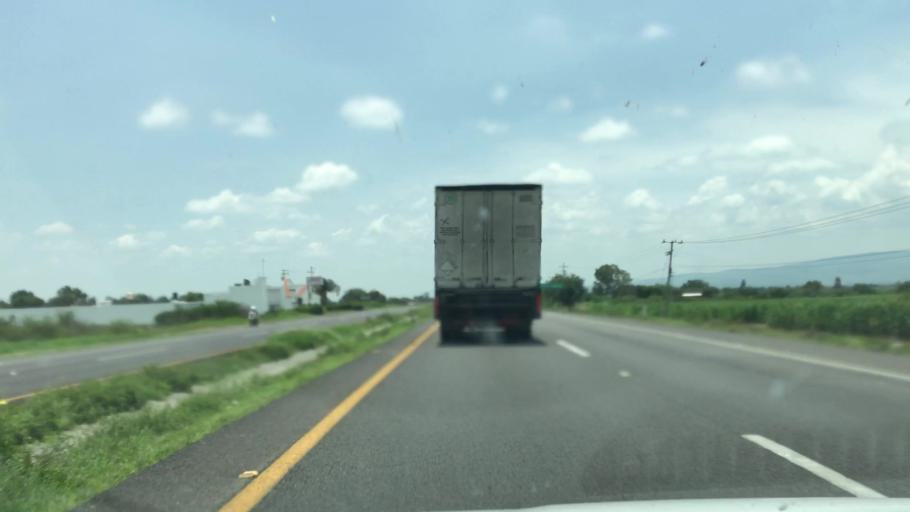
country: MX
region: Guanajuato
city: Penjamo
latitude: 20.4417
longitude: -101.6677
